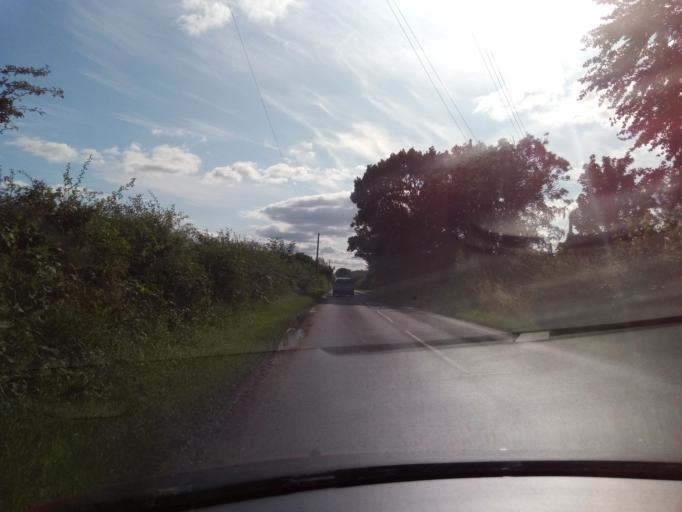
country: GB
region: Scotland
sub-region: The Scottish Borders
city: Allanton
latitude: 55.7519
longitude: -2.1529
